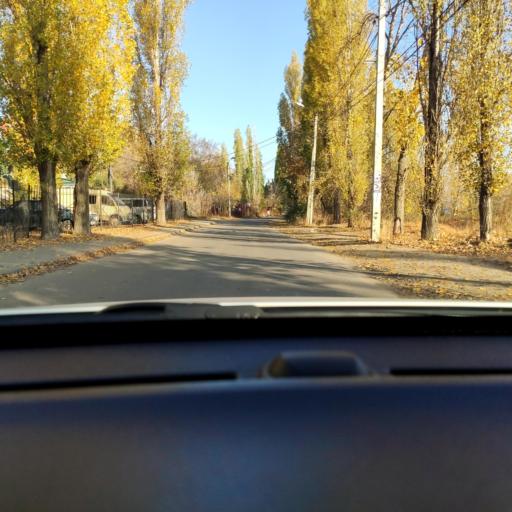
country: RU
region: Voronezj
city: Voronezh
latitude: 51.6956
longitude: 39.2339
